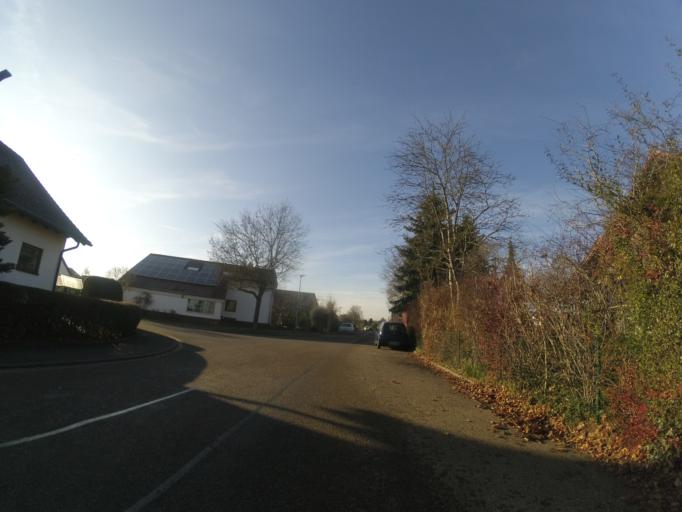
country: DE
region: Baden-Wuerttemberg
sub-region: Tuebingen Region
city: Dornstadt
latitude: 48.4588
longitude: 9.9112
